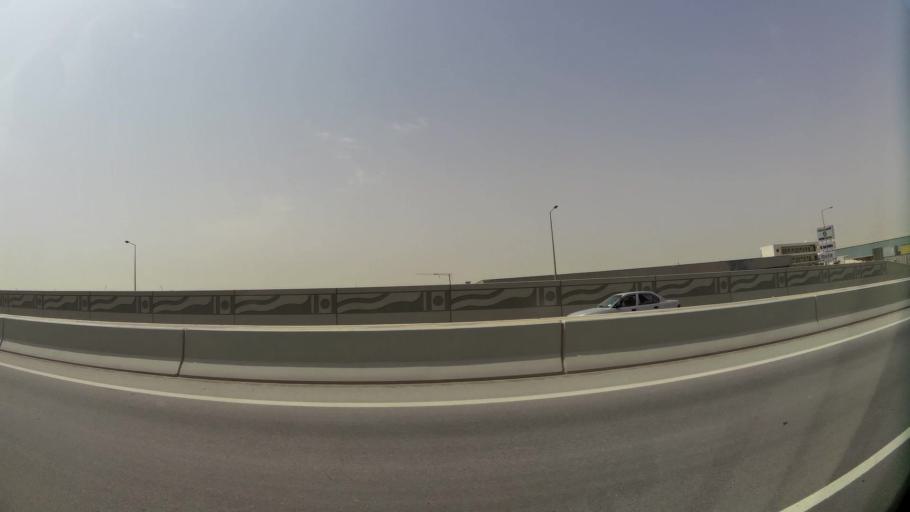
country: QA
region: Baladiyat ar Rayyan
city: Ar Rayyan
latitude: 25.2054
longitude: 51.4463
